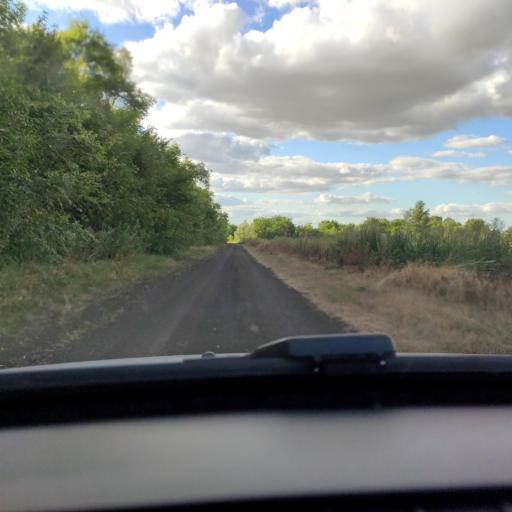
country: RU
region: Voronezj
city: Verkhnyaya Khava
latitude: 51.6045
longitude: 39.8380
